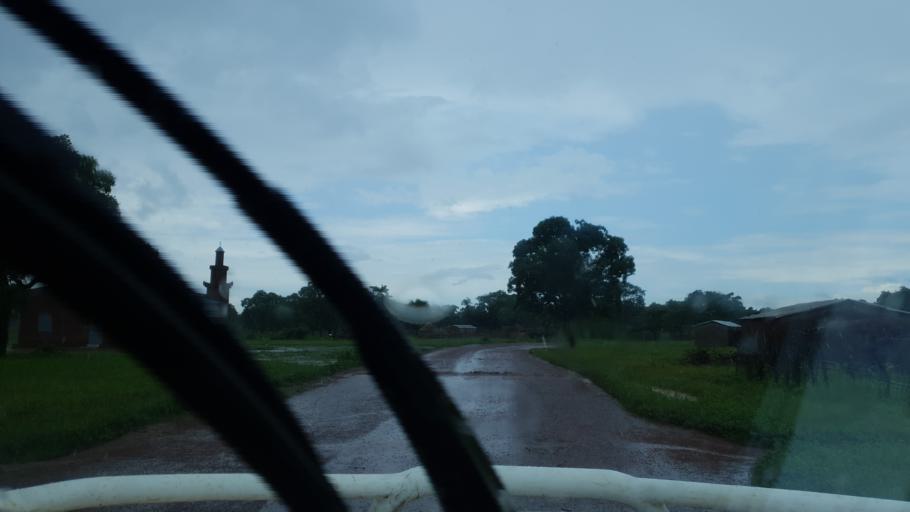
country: ML
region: Sikasso
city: Kolondieba
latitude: 11.5963
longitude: -6.6619
